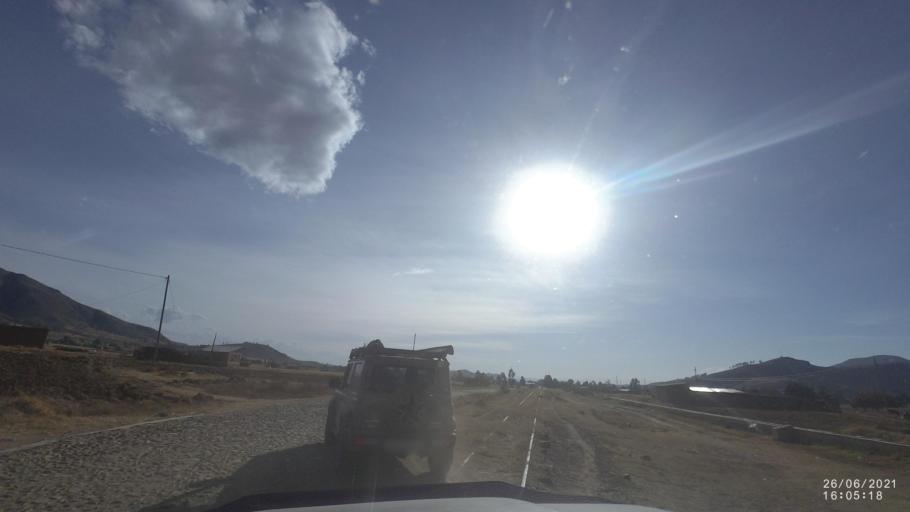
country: BO
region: Cochabamba
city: Arani
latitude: -17.8291
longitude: -65.7612
